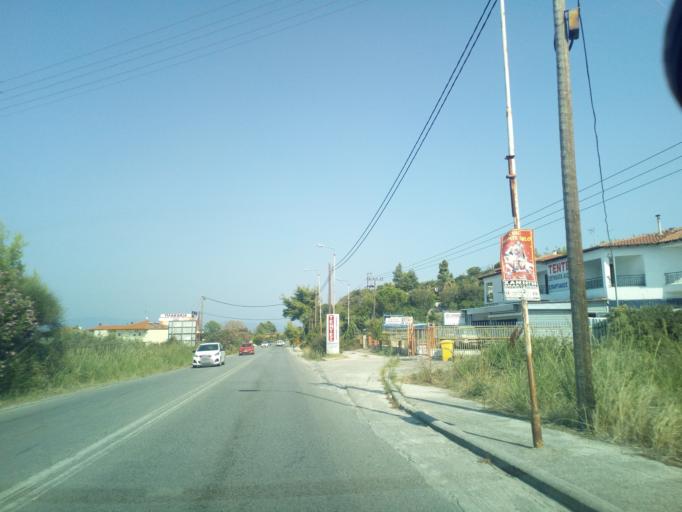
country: GR
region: Central Macedonia
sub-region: Nomos Chalkidikis
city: Pefkochori
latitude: 40.0136
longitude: 23.5327
